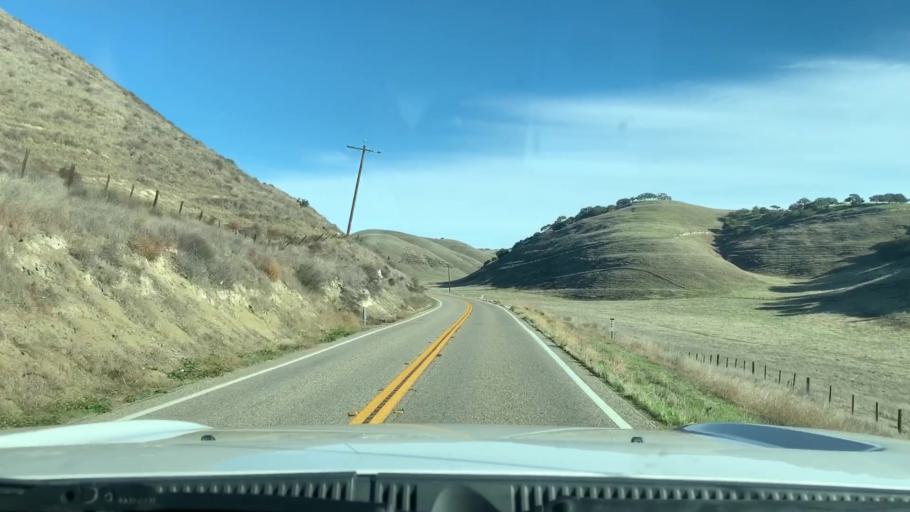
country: US
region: California
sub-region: Monterey County
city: King City
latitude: 36.1683
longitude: -120.8525
